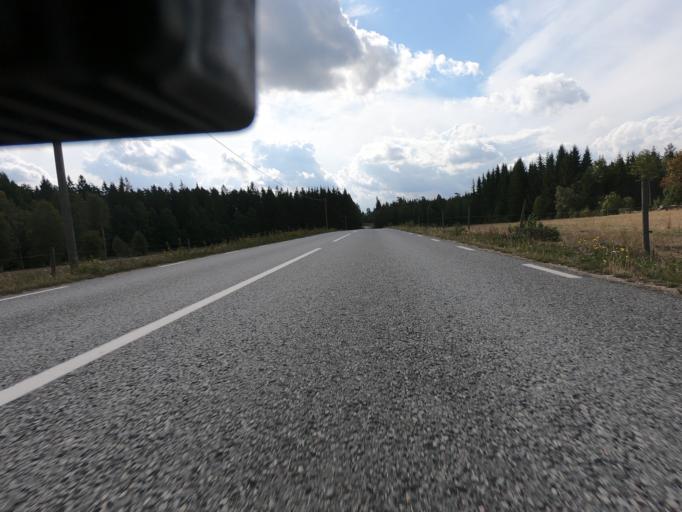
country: SE
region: Joenkoeping
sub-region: Vetlanda Kommun
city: Landsbro
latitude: 57.2996
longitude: 14.8711
